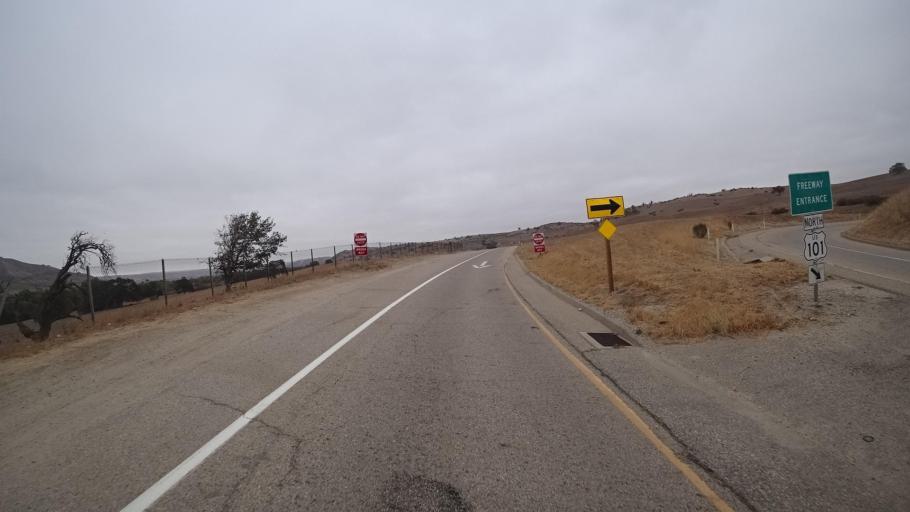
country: US
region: California
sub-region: San Luis Obispo County
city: Lake Nacimiento
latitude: 35.8729
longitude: -120.8319
